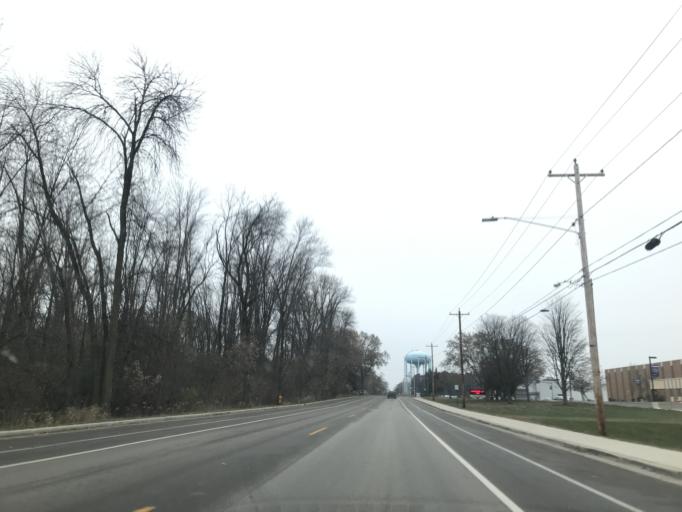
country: US
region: Wisconsin
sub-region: Marinette County
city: Marinette
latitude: 45.0832
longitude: -87.6296
